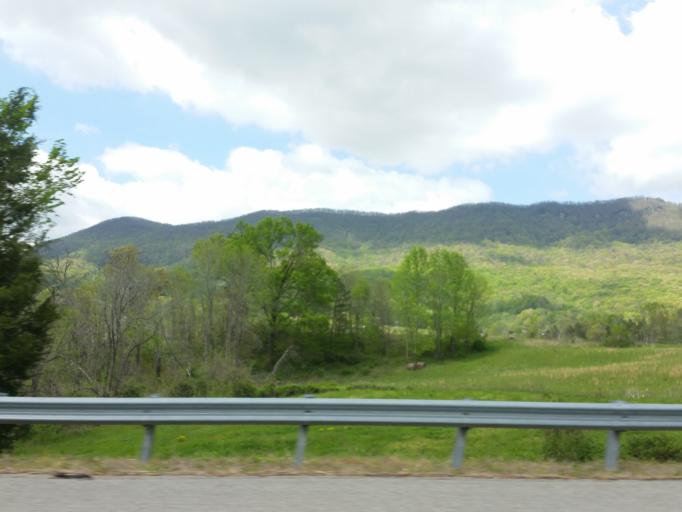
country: US
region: Tennessee
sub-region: Campbell County
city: Fincastle
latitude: 36.4477
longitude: -83.9353
